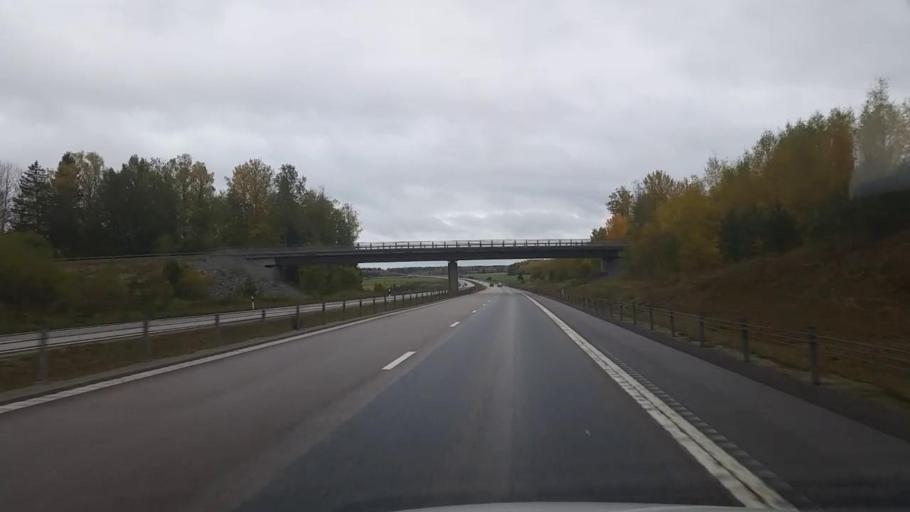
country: SE
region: Uppsala
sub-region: Osthammars Kommun
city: Bjorklinge
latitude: 60.1370
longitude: 17.5470
